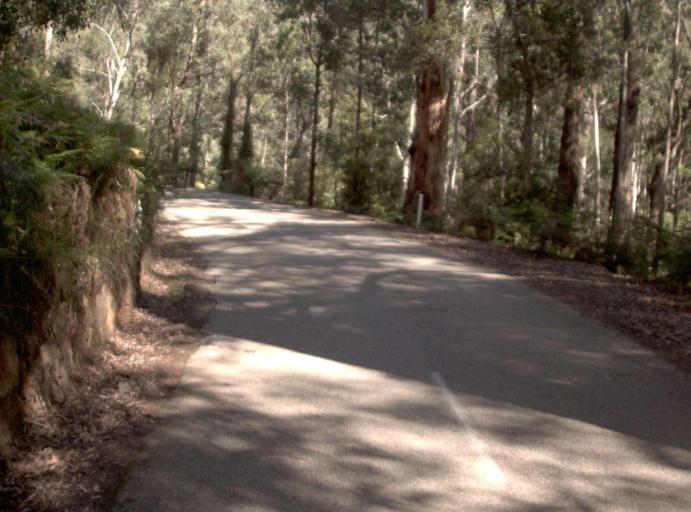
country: AU
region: Victoria
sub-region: East Gippsland
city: Lakes Entrance
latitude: -37.4118
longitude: 148.5974
